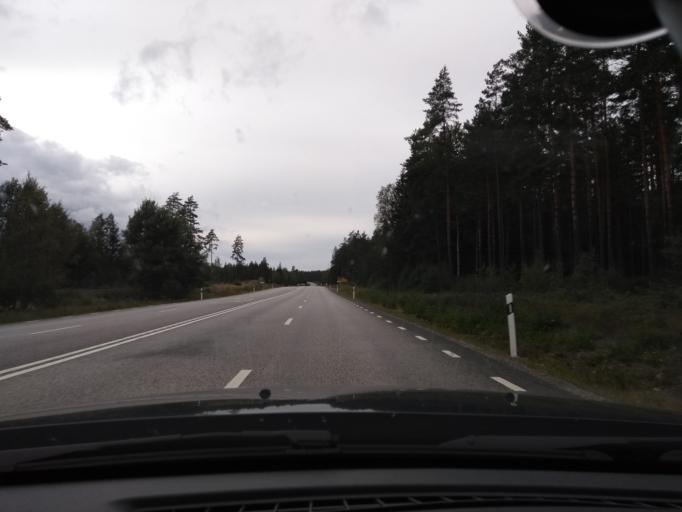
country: SE
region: OEstergoetland
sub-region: Ydre Kommun
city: OEsterbymo
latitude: 57.6440
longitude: 15.1778
